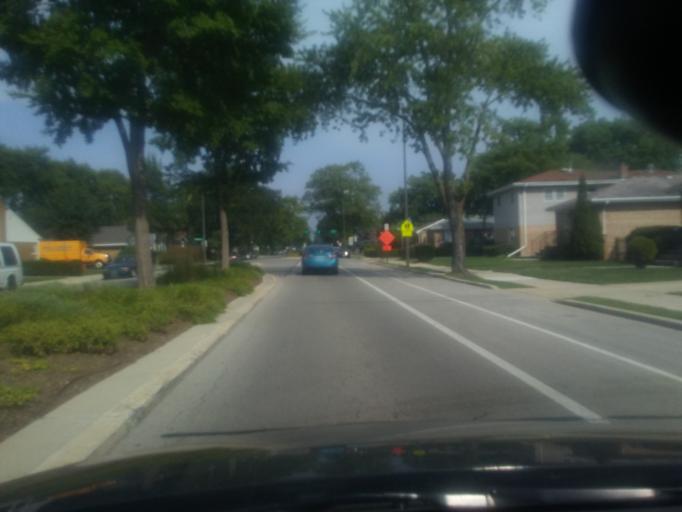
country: US
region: Illinois
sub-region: Cook County
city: Skokie
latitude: 42.0334
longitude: -87.7204
